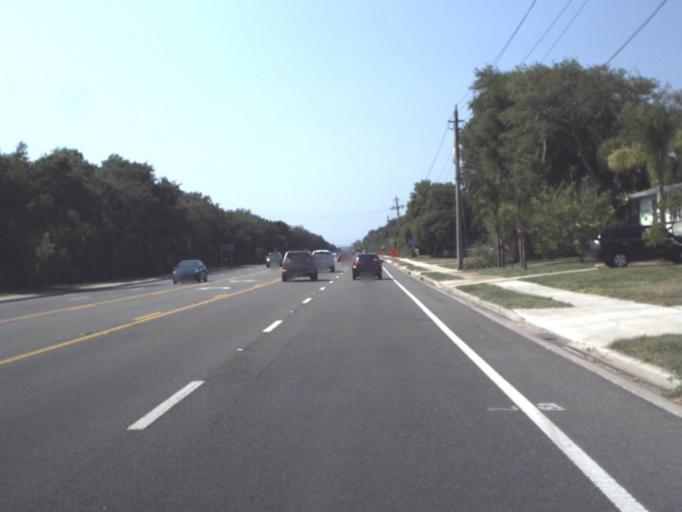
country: US
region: Florida
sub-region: Saint Johns County
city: Saint Augustine
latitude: 29.8781
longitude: -81.2861
